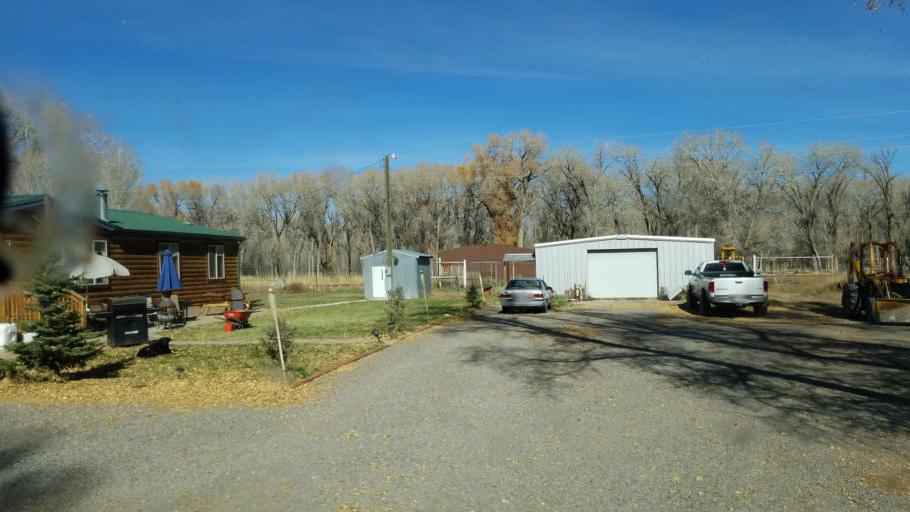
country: US
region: Colorado
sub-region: Conejos County
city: Conejos
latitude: 37.0613
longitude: -106.0953
